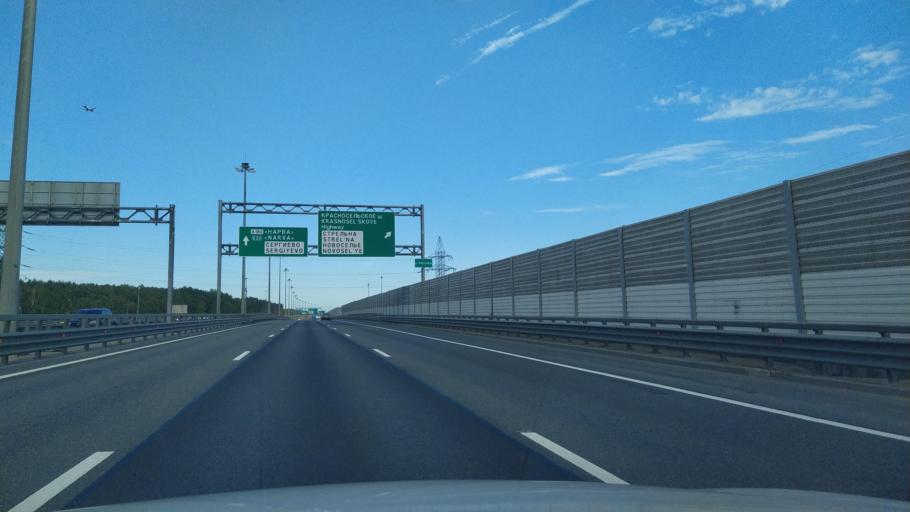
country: RU
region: St.-Petersburg
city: Strel'na
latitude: 59.8169
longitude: 30.0520
